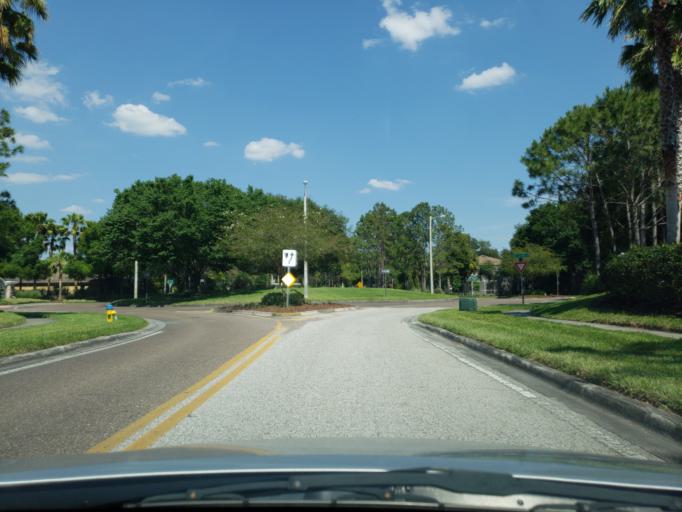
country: US
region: Florida
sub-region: Hillsborough County
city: Riverview
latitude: 27.8697
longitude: -82.3560
